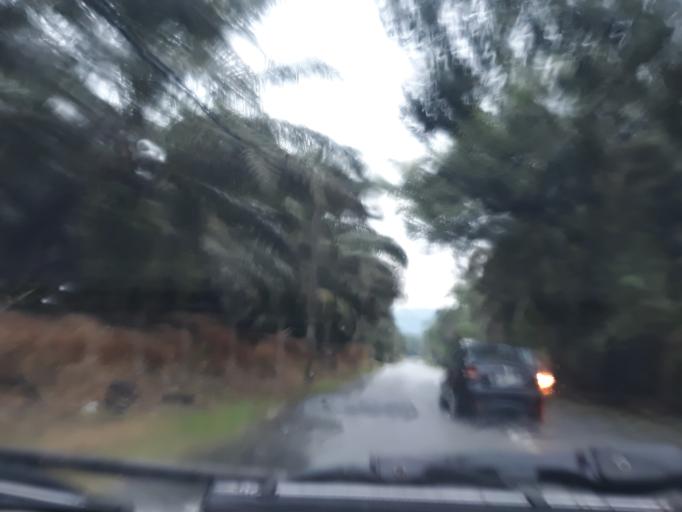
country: MY
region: Kedah
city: Kulim
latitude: 5.2346
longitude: 100.6033
